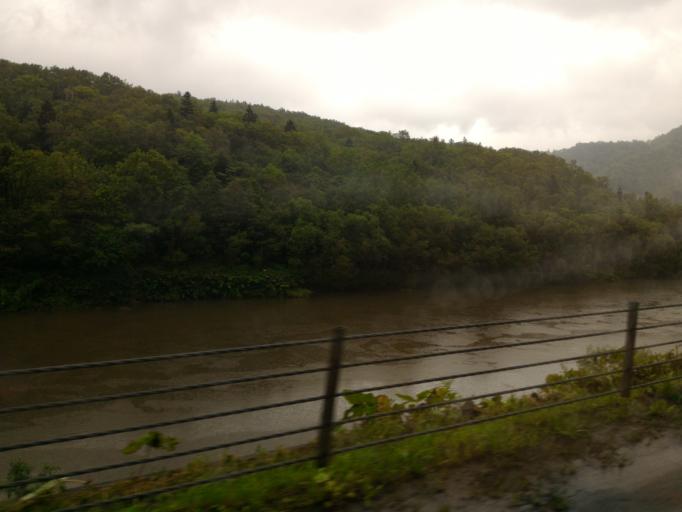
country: JP
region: Hokkaido
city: Nayoro
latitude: 44.7247
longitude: 142.1683
